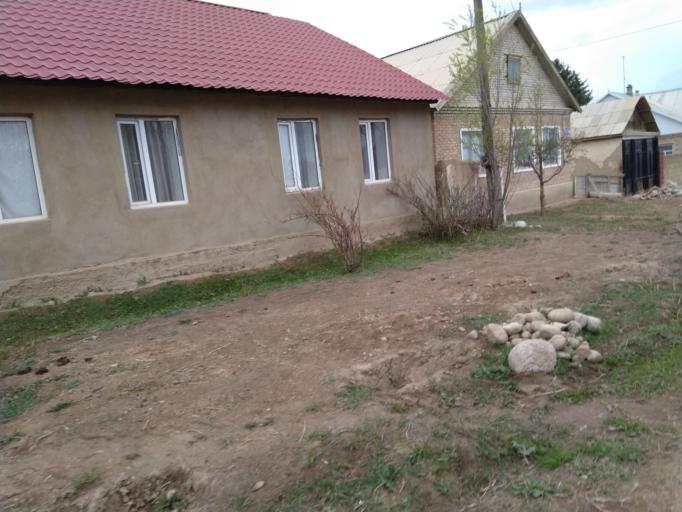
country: KG
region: Ysyk-Koel
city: Bokombayevskoye
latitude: 42.1093
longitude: 76.9825
